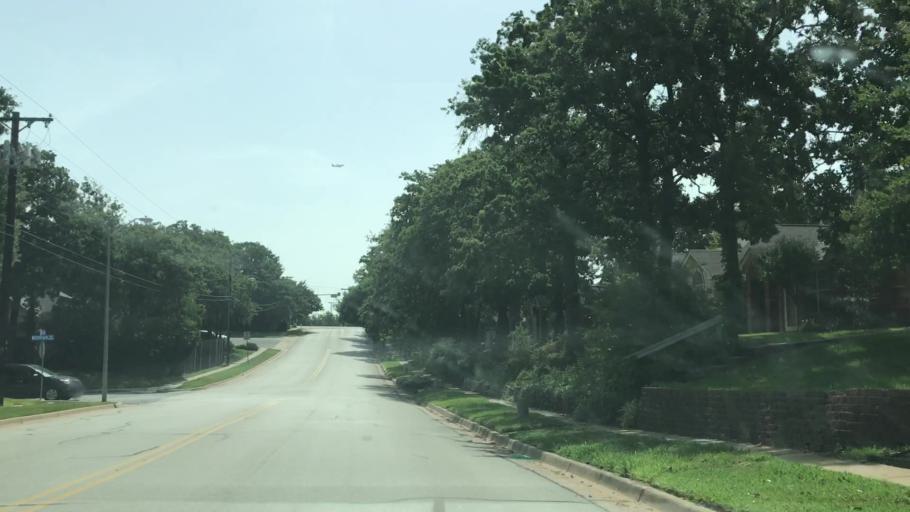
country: US
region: Texas
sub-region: Tarrant County
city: Euless
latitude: 32.8590
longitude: -97.0759
